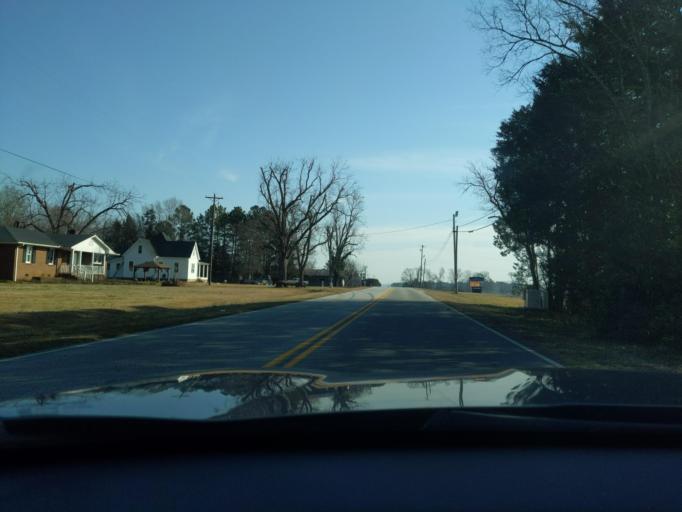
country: US
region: South Carolina
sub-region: Abbeville County
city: Calhoun Falls
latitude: 34.0926
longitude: -82.5770
